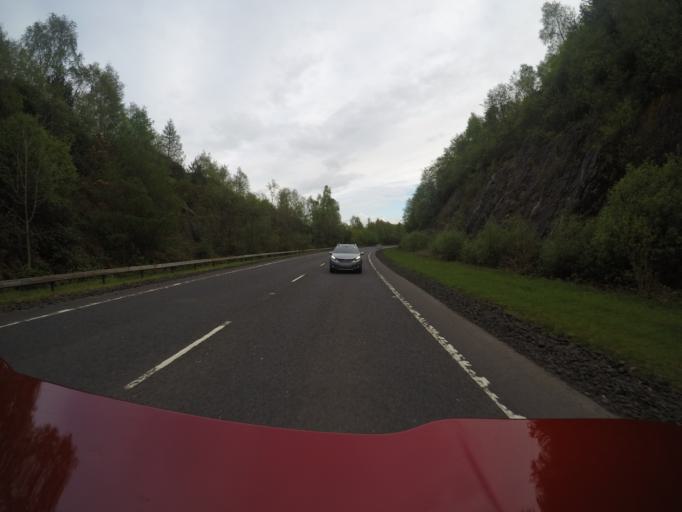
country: GB
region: Scotland
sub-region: West Dunbartonshire
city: Balloch
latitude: 56.0870
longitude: -4.6394
